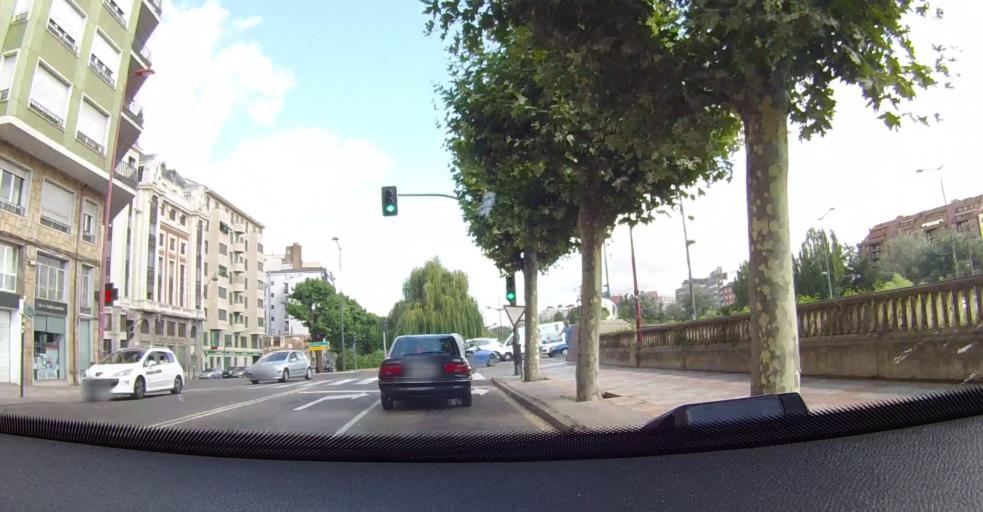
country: ES
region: Castille and Leon
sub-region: Provincia de Leon
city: Leon
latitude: 42.5955
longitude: -5.5797
